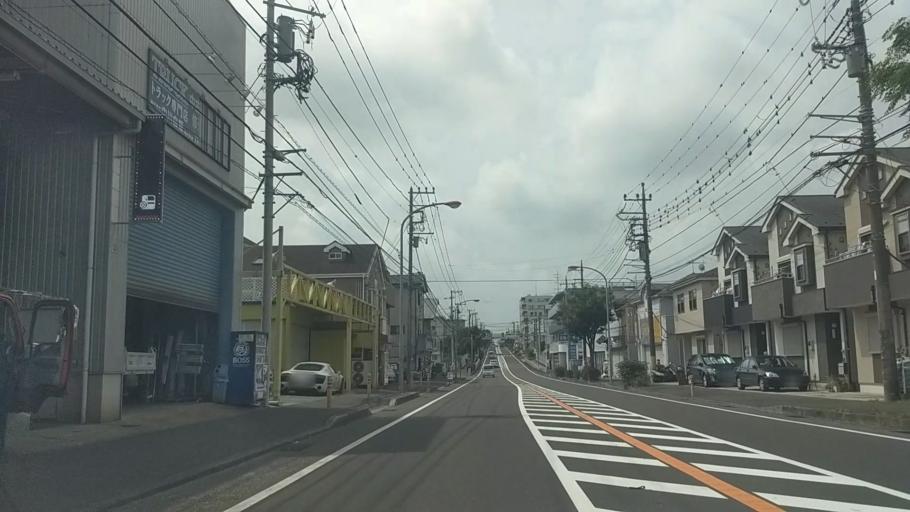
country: JP
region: Kanagawa
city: Fujisawa
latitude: 35.3696
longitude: 139.4790
